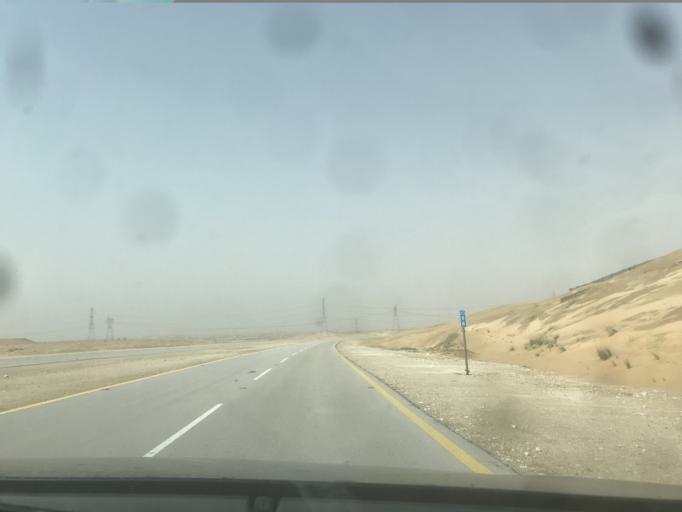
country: SA
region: Eastern Province
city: Abqaiq
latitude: 25.9255
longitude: 49.7614
